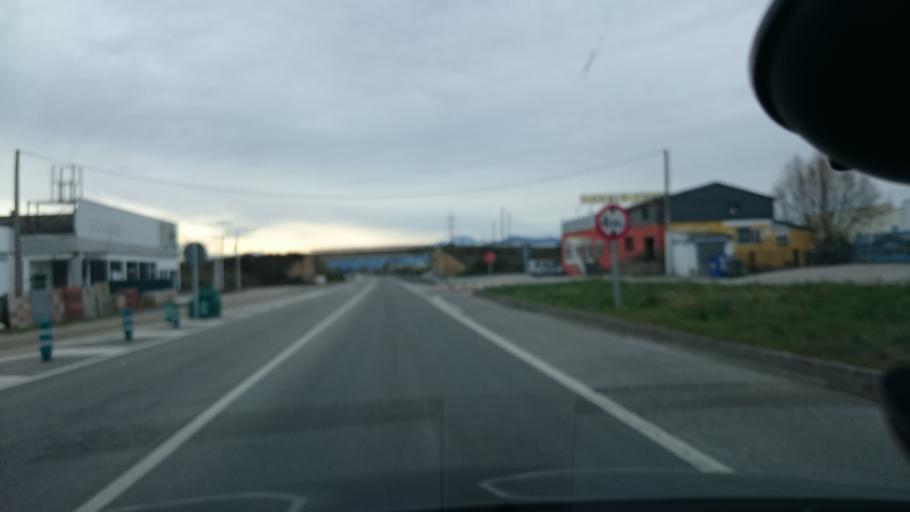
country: ES
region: Castille and Leon
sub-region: Provincia de Leon
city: Camponaraya
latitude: 42.5660
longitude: -6.6597
